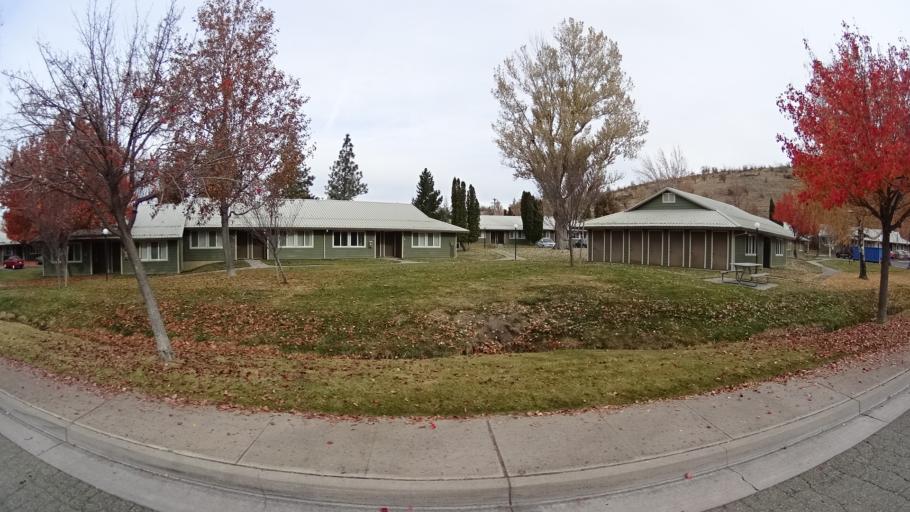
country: US
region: California
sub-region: Siskiyou County
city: Weed
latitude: 41.4226
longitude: -122.3827
